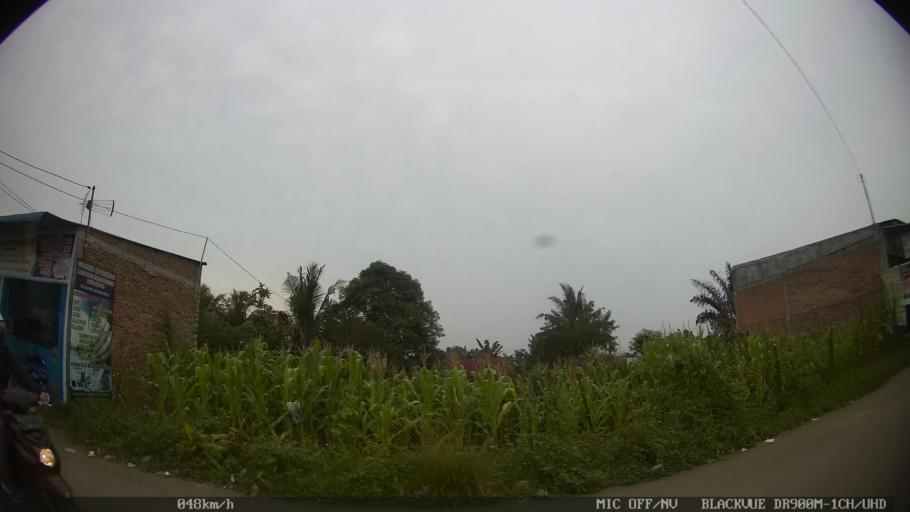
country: ID
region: North Sumatra
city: Deli Tua
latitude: 3.5383
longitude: 98.7351
